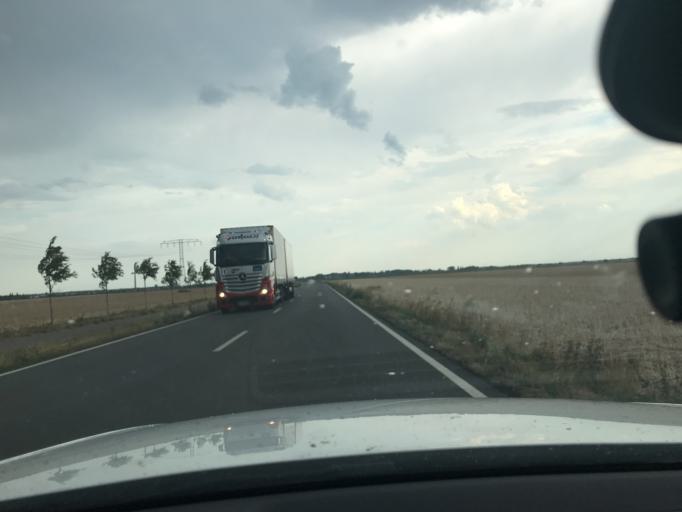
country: DE
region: Saxony
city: Markranstadt
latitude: 51.3268
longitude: 12.2070
